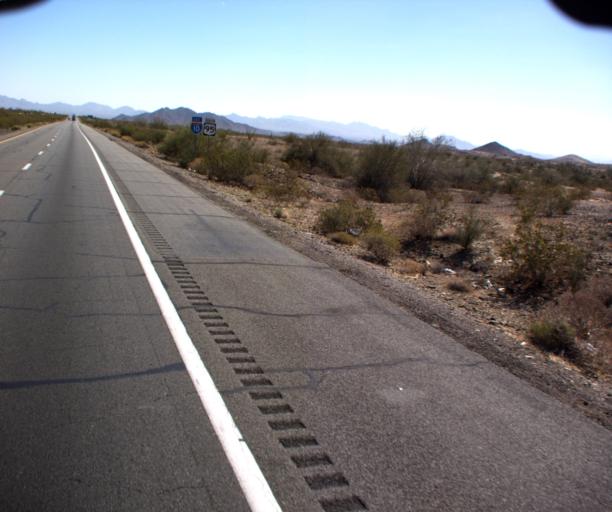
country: US
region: Arizona
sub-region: La Paz County
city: Quartzsite
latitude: 33.6470
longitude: -114.3287
